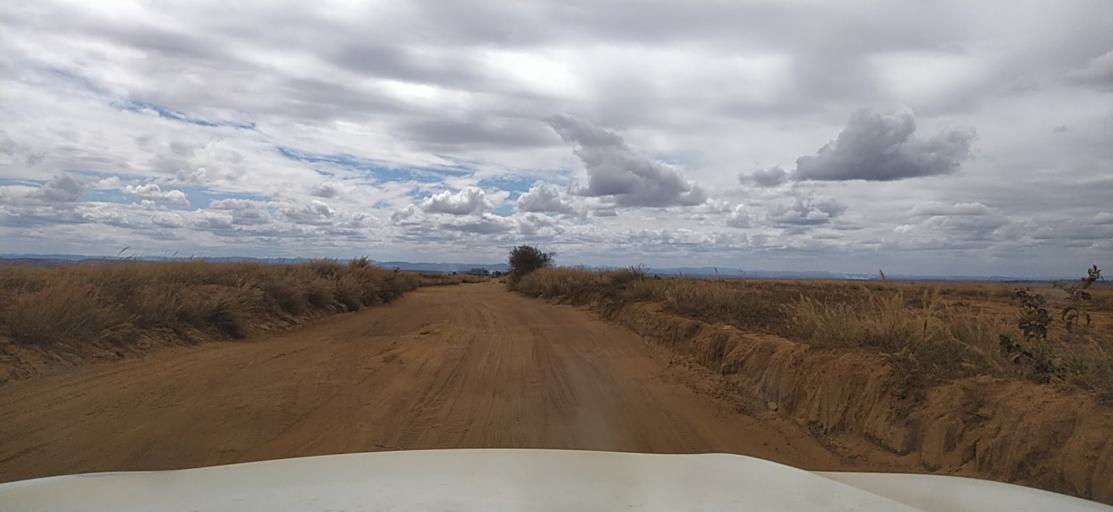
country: MG
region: Alaotra Mangoro
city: Ambatondrazaka
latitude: -17.9121
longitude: 48.2656
